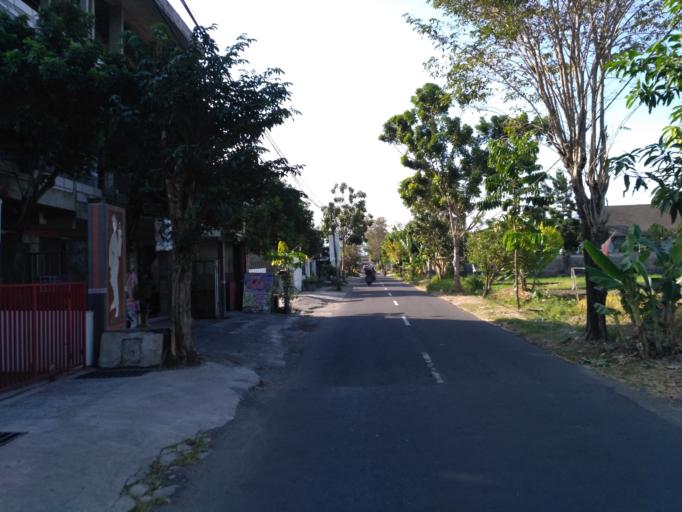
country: ID
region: Daerah Istimewa Yogyakarta
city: Depok
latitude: -7.7770
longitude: 110.4234
